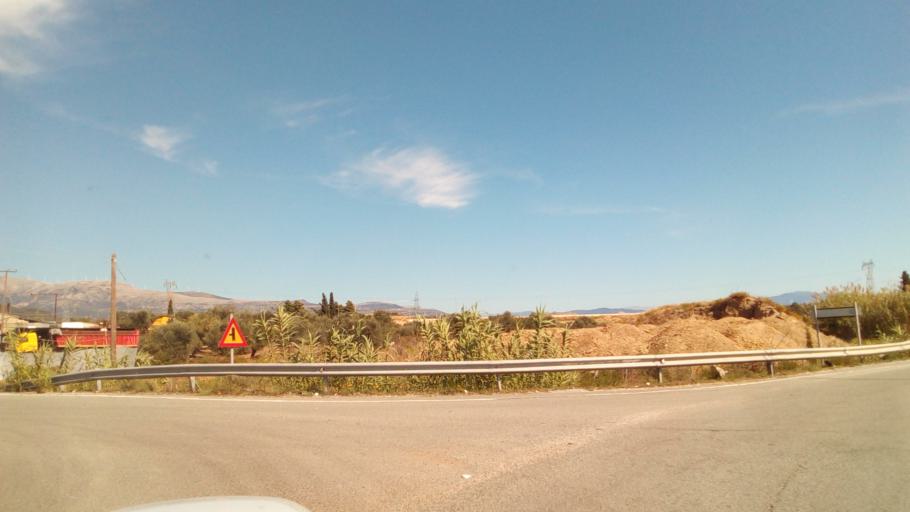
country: GR
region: West Greece
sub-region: Nomos Aitolias kai Akarnanias
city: Antirrio
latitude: 38.3396
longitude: 21.7557
